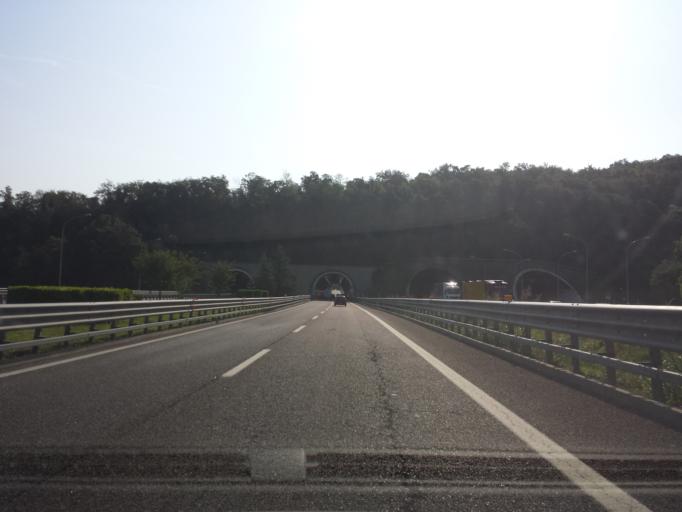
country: IT
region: Veneto
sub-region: Provincia di Vicenza
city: Arcugnano-Torri
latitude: 45.5175
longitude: 11.5311
